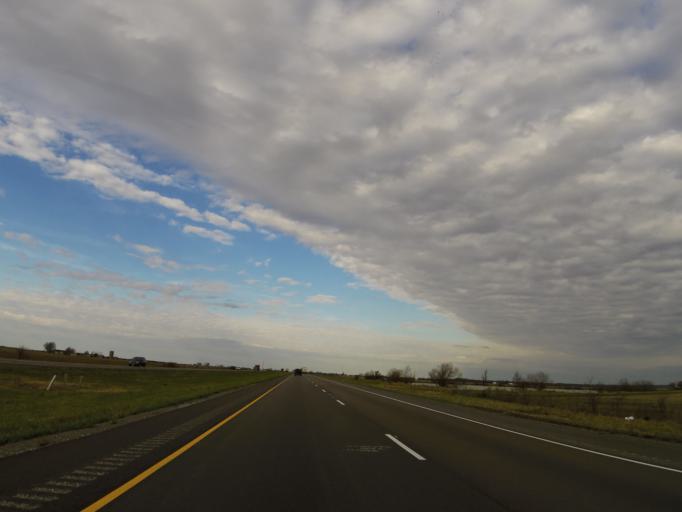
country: US
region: Illinois
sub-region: Washington County
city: Okawville
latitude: 38.4226
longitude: -89.4540
